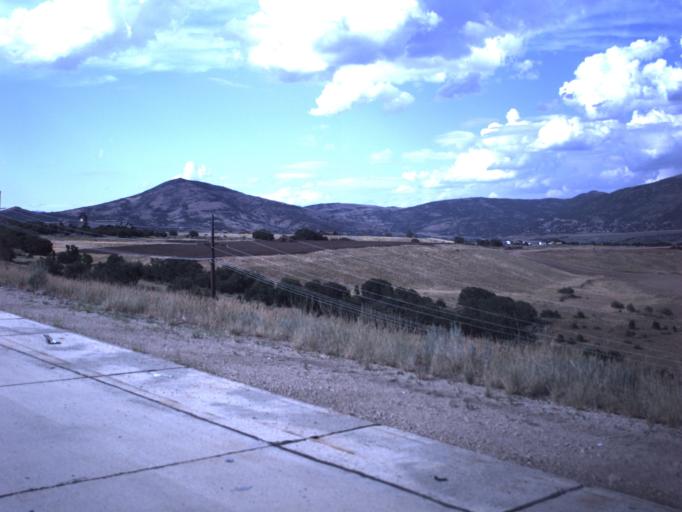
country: US
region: Utah
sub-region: Summit County
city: Park City
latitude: 40.6197
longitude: -111.4369
